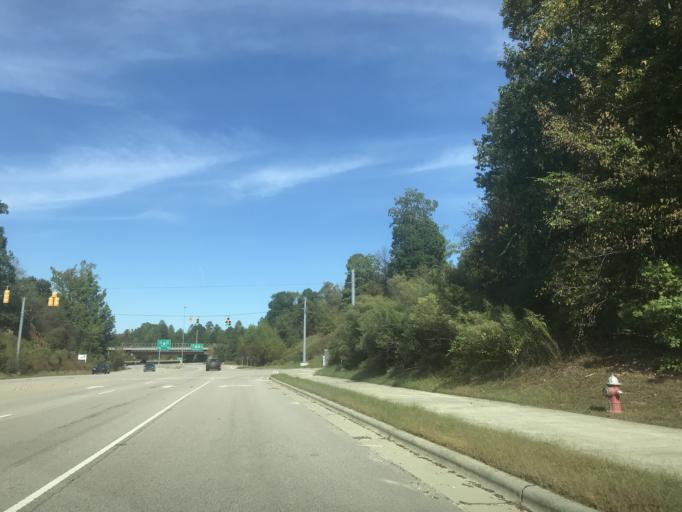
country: US
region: North Carolina
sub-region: Wake County
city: Raleigh
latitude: 35.8705
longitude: -78.5700
